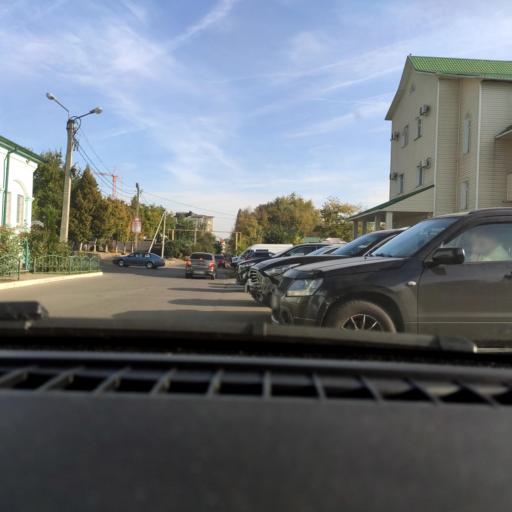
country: RU
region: Voronezj
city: Voronezh
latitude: 51.6529
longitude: 39.2093
